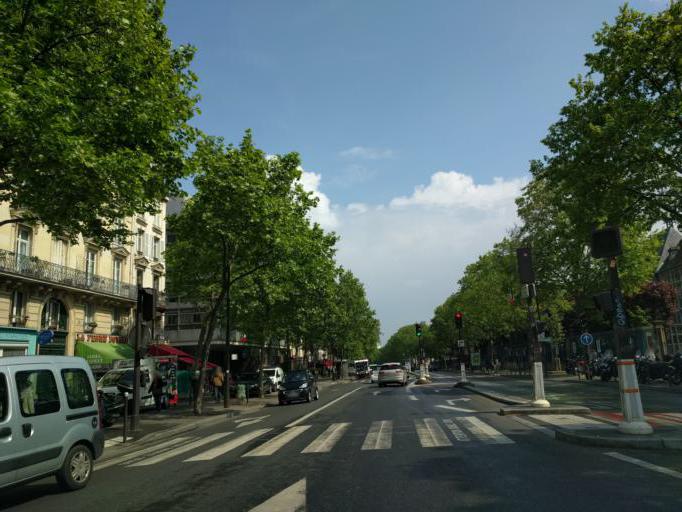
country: FR
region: Ile-de-France
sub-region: Paris
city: Paris
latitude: 48.8394
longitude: 2.3377
